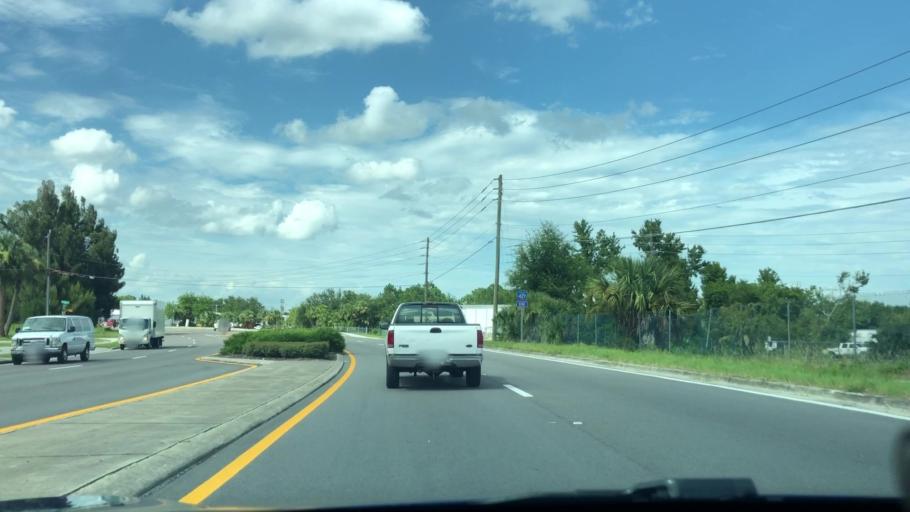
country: US
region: Florida
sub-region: Seminole County
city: Sanford
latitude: 28.7608
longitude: -81.2651
